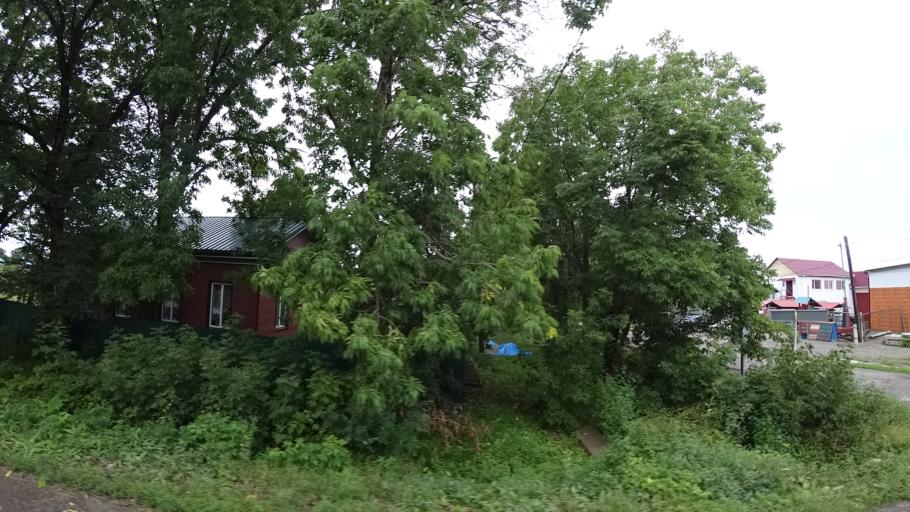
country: RU
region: Primorskiy
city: Chernigovka
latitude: 44.3462
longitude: 132.5697
